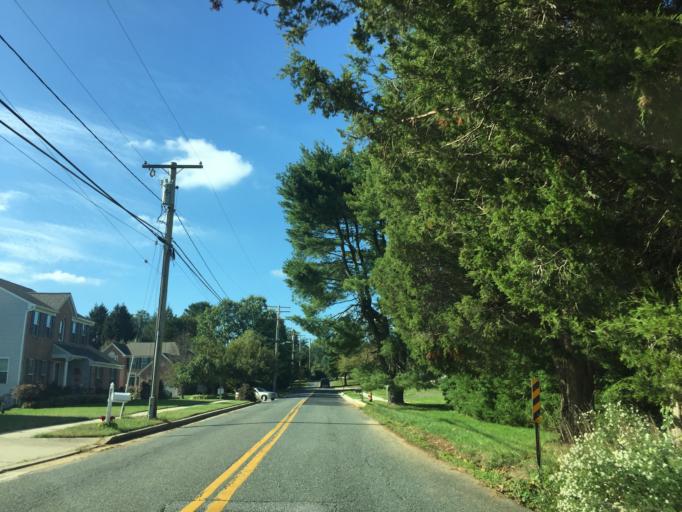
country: US
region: Maryland
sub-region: Baltimore County
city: Perry Hall
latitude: 39.4222
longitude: -76.4631
